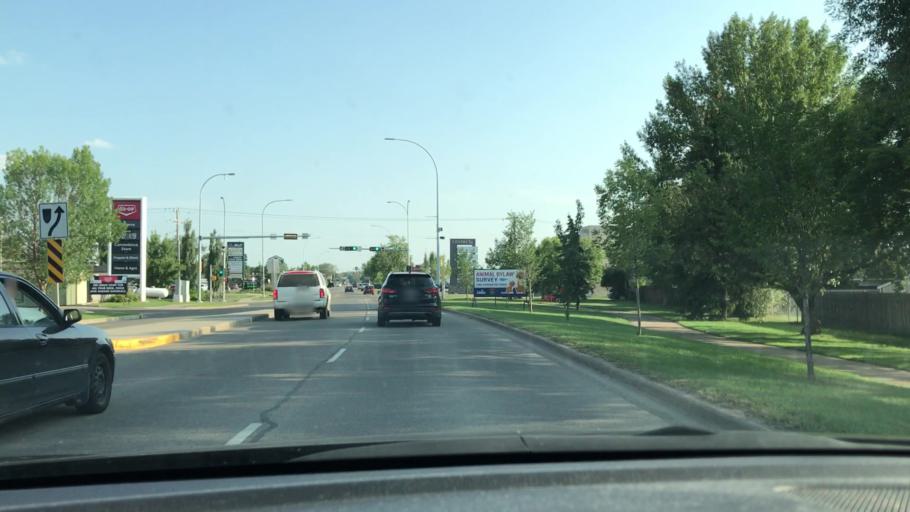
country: CA
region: Alberta
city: Leduc
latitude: 53.2692
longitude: -113.5525
